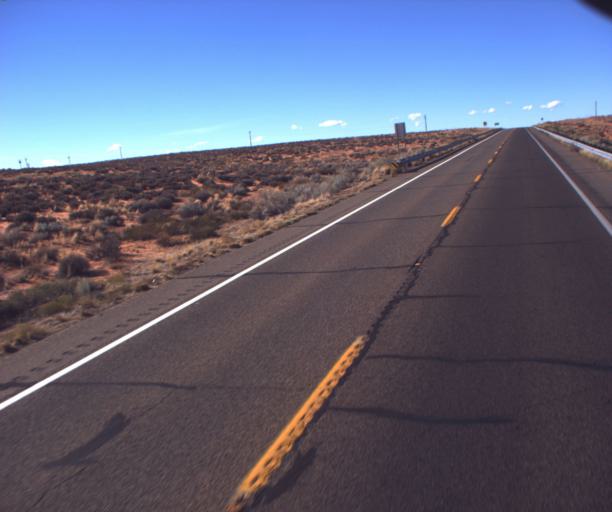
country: US
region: Arizona
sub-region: Coconino County
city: Page
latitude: 36.9559
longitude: -111.5024
